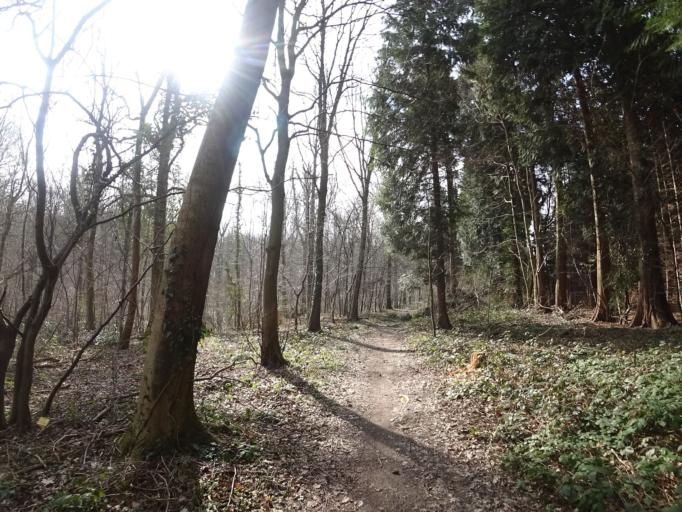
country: BE
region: Wallonia
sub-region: Province de Namur
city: Namur
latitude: 50.4349
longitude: 4.8289
